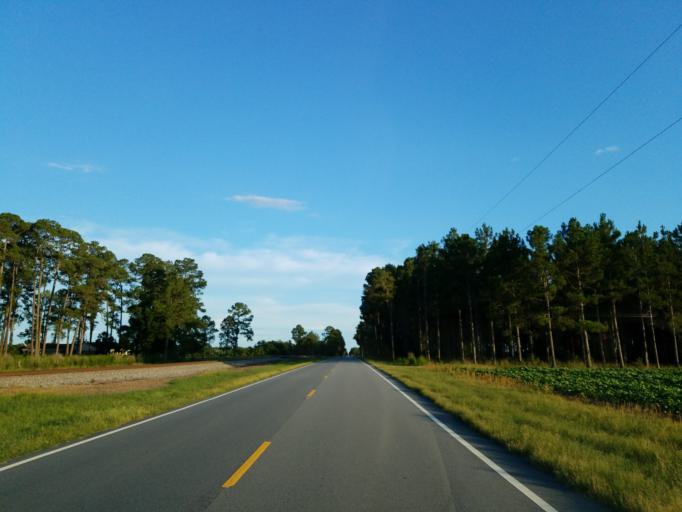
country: US
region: Georgia
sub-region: Tift County
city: Unionville
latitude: 31.3426
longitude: -83.4824
